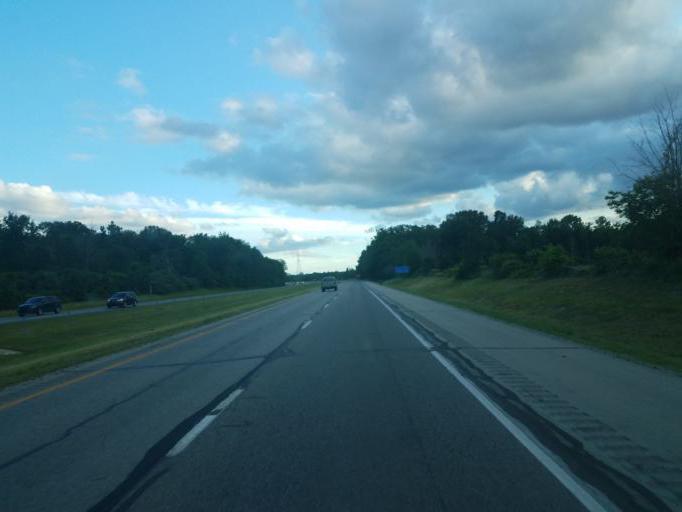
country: US
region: Indiana
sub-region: Allen County
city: Leo-Cedarville
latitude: 41.2527
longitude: -85.0898
